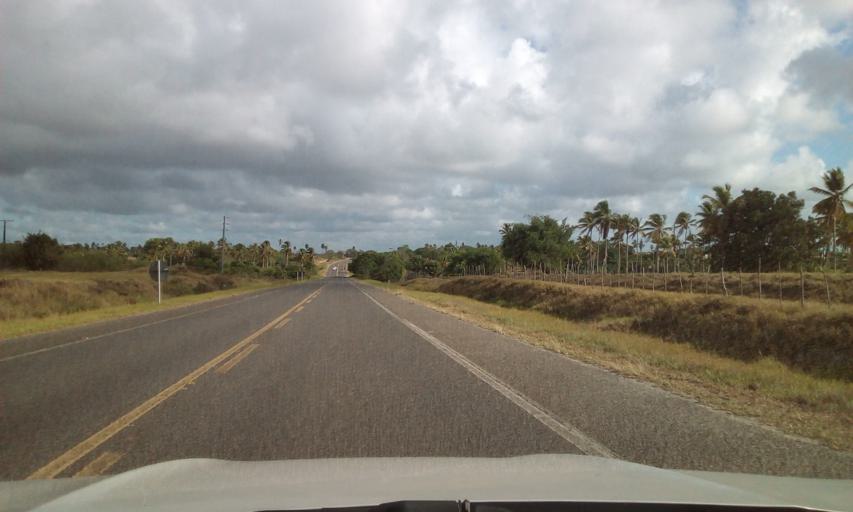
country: BR
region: Bahia
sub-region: Conde
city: Conde
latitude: -11.8229
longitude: -37.6354
